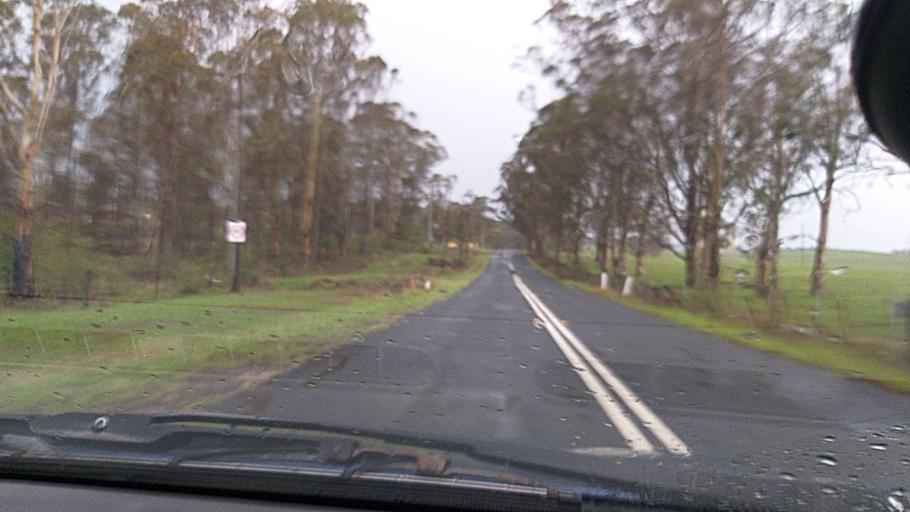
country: AU
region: New South Wales
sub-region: Wollondilly
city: Douglas Park
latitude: -34.2061
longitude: 150.7194
